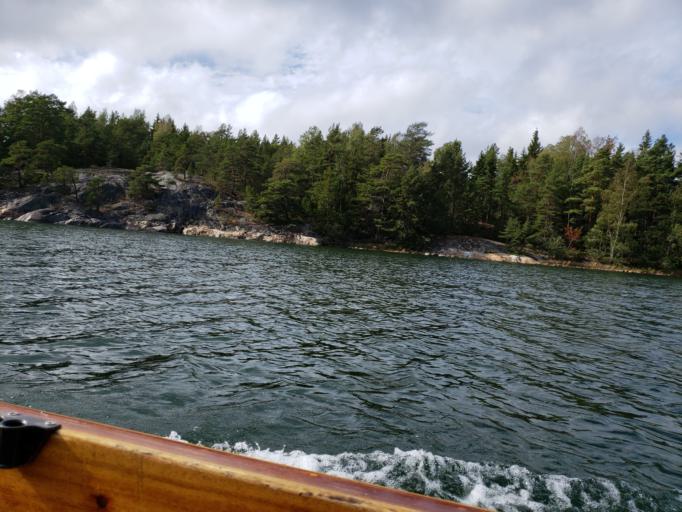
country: FI
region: Varsinais-Suomi
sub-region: Aboland-Turunmaa
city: Dragsfjaerd
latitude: 59.9156
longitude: 22.3817
